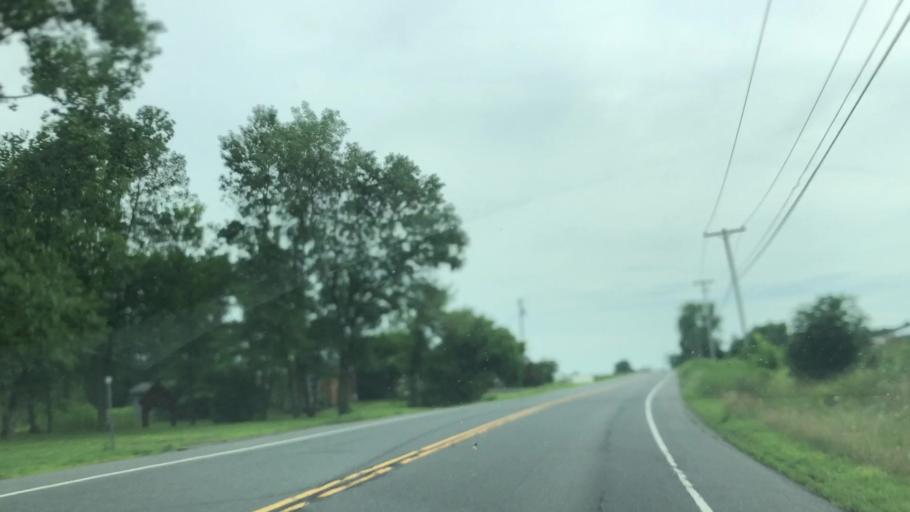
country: US
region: New York
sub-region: Washington County
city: Whitehall
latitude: 43.5185
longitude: -73.4143
